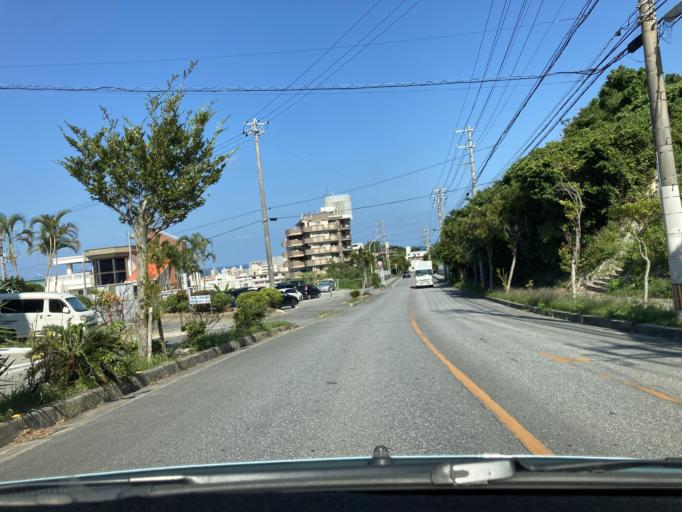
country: JP
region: Okinawa
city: Ginowan
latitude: 26.2535
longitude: 127.7247
